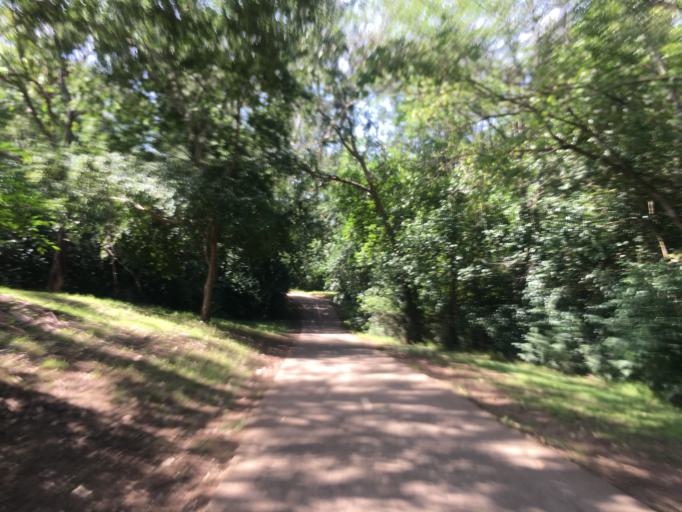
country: AU
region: New South Wales
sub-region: Camden
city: Elderslie
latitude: -34.0625
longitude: 150.7002
